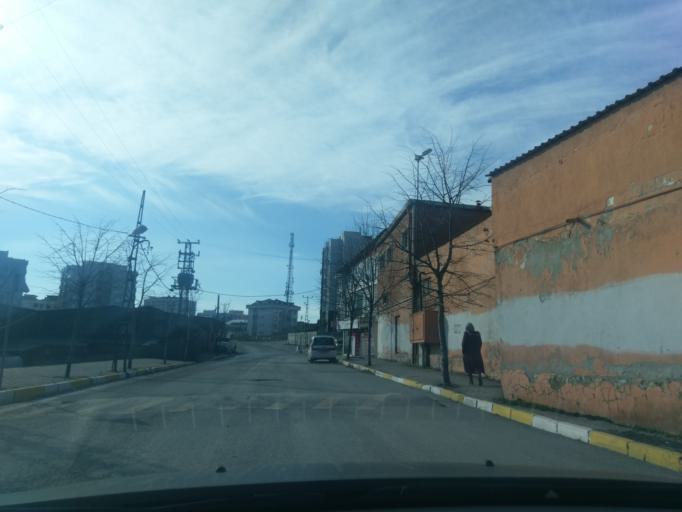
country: TR
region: Istanbul
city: Sultangazi
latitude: 41.1331
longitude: 28.8389
